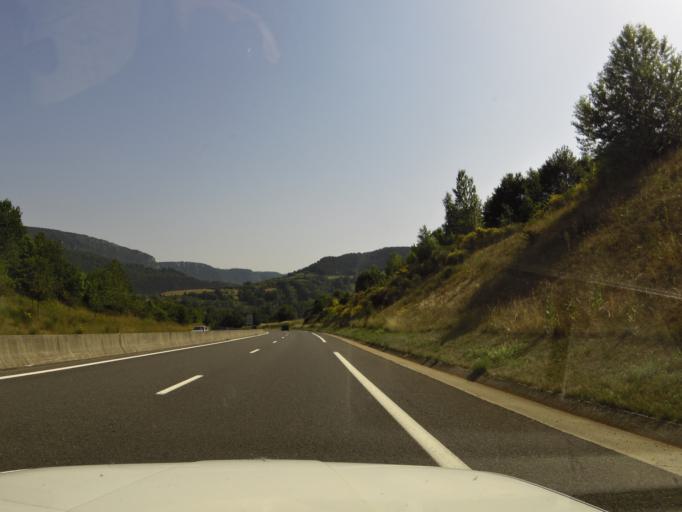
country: FR
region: Languedoc-Roussillon
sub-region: Departement de la Lozere
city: La Canourgue
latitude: 44.4444
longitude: 3.1943
